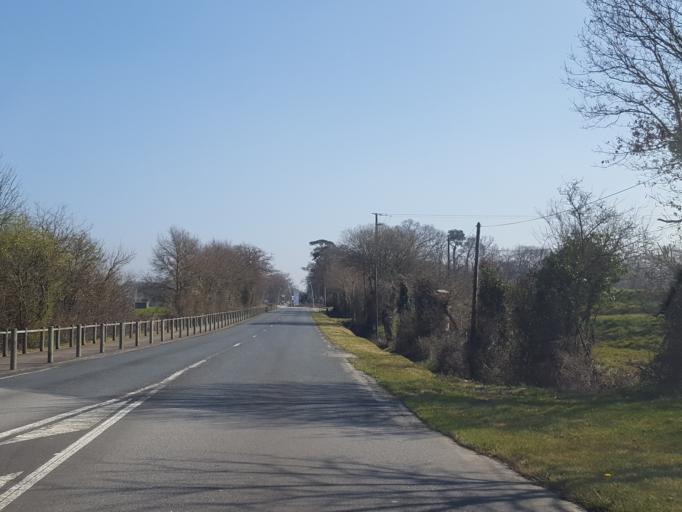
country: FR
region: Pays de la Loire
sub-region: Departement de la Vendee
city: La Ferriere
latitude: 46.6645
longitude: -1.3618
